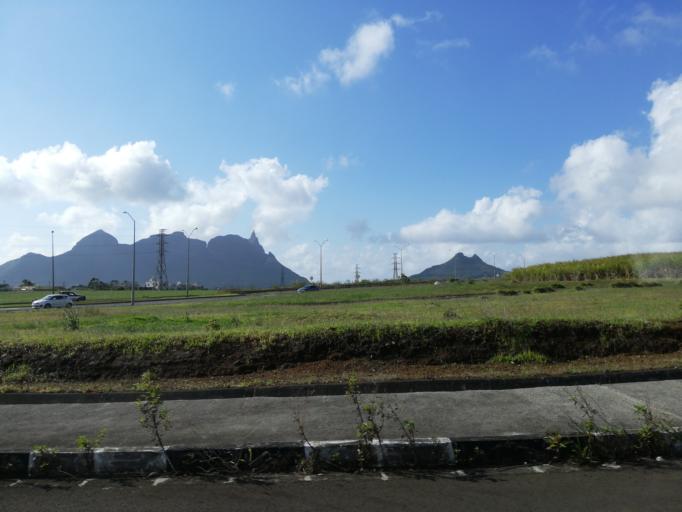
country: MU
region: Moka
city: Verdun
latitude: -20.2245
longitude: 57.5587
